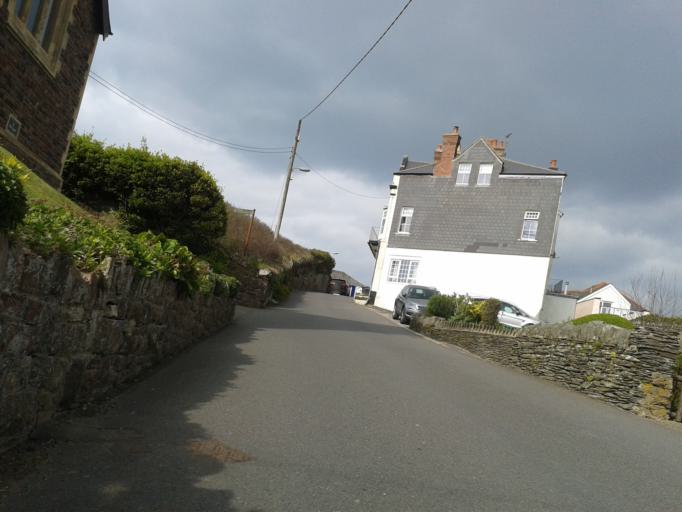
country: GB
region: England
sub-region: Devon
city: Braunton
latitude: 51.1839
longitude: -4.2098
